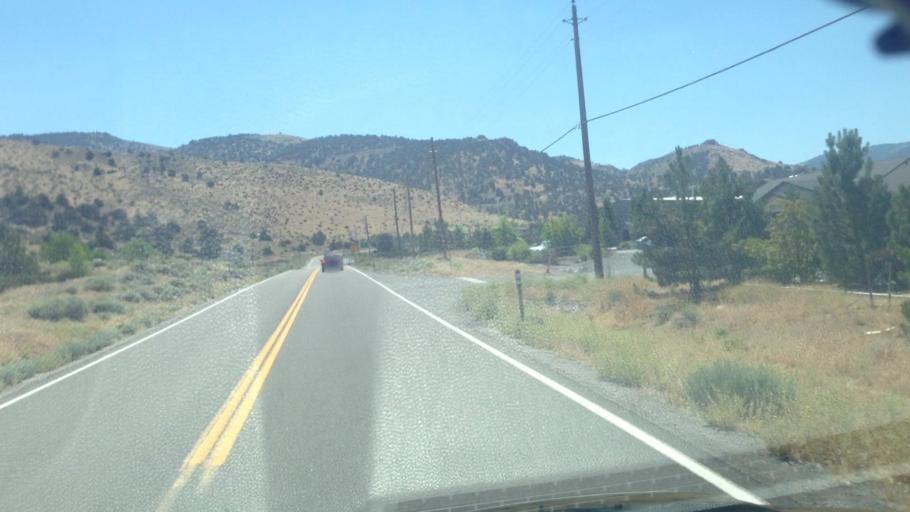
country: US
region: Nevada
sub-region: Storey County
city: Virginia City
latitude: 39.3920
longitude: -119.7212
